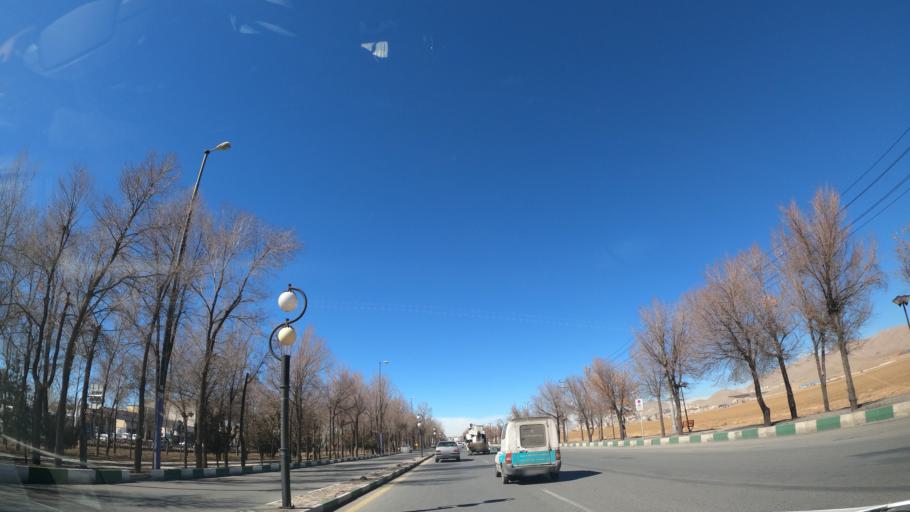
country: IR
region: Chahar Mahall va Bakhtiari
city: Shahrekord
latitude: 32.3080
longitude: 50.9000
